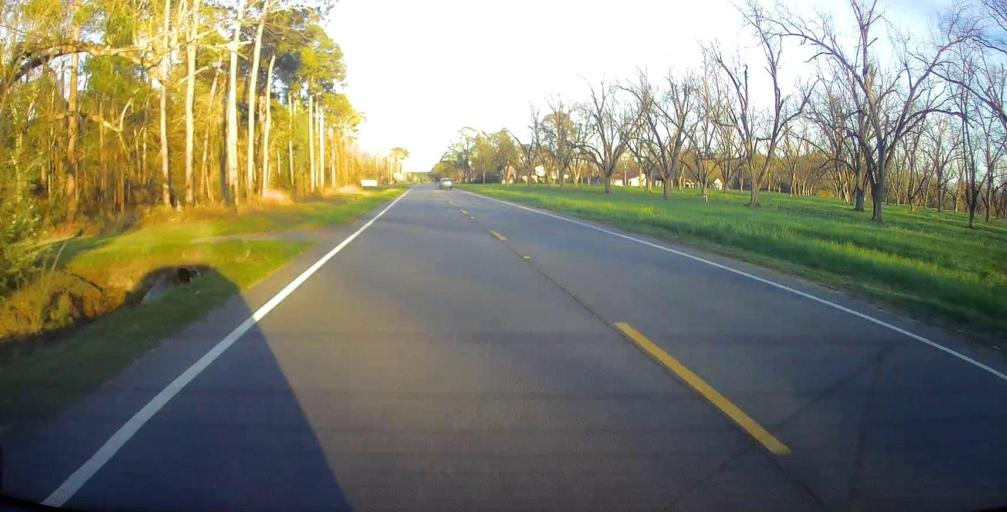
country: US
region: Georgia
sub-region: Crisp County
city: Cordele
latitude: 31.9577
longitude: -83.7389
